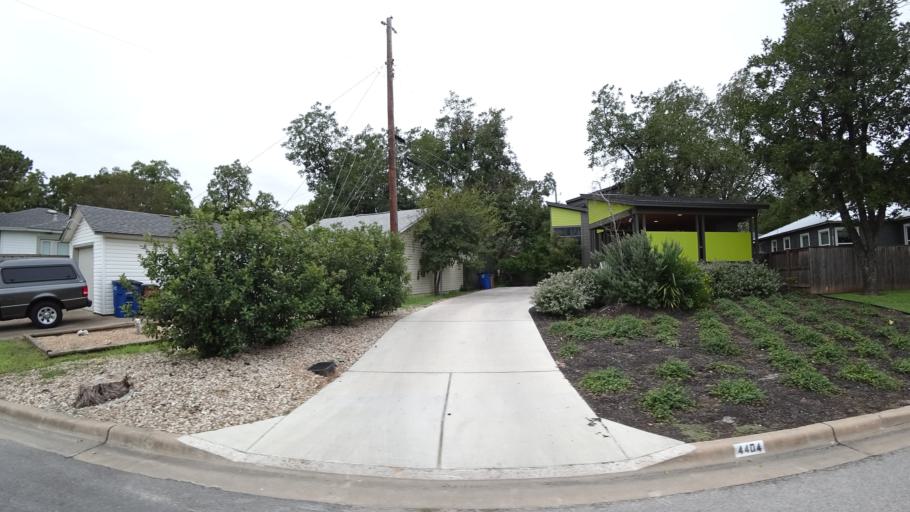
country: US
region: Texas
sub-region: Travis County
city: Austin
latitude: 30.3021
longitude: -97.7166
